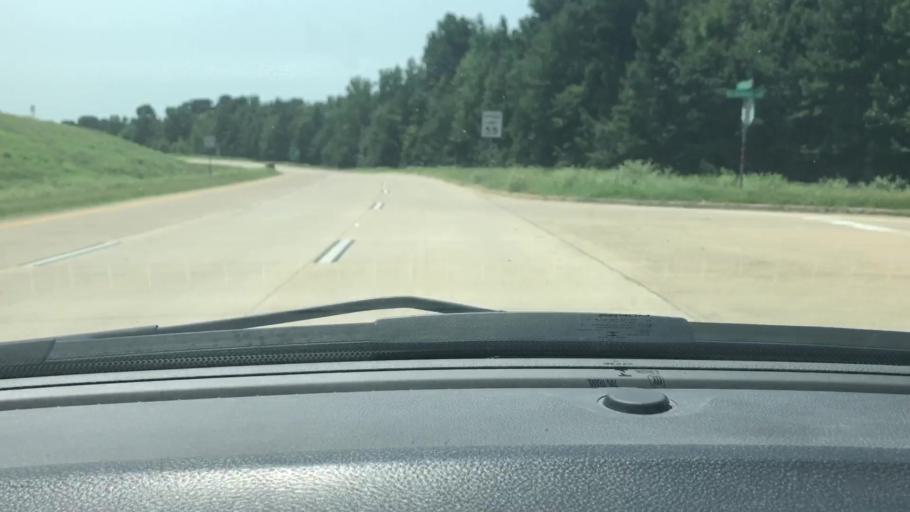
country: US
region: Texas
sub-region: Bowie County
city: Wake Village
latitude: 33.3927
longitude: -94.0988
